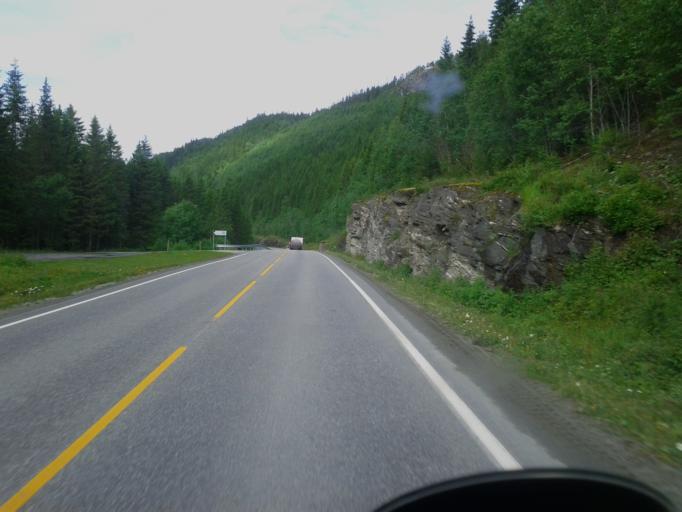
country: NO
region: Nord-Trondelag
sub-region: Grong
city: Grong
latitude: 64.5367
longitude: 12.4338
